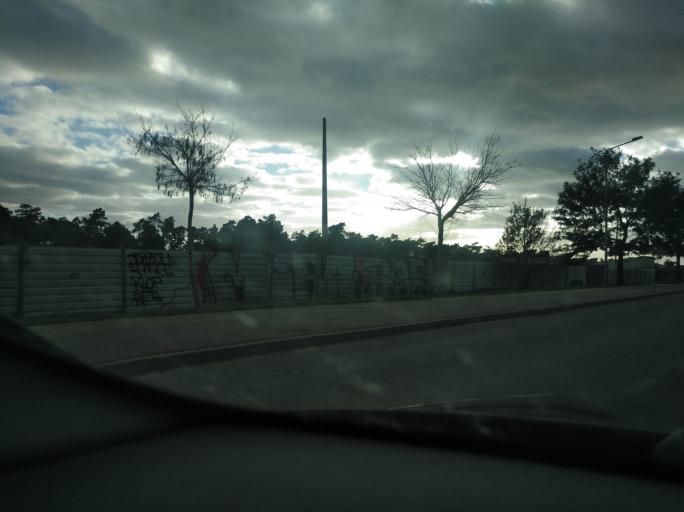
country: PT
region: Faro
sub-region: Vila Real de Santo Antonio
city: Monte Gordo
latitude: 37.1863
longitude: -7.4548
